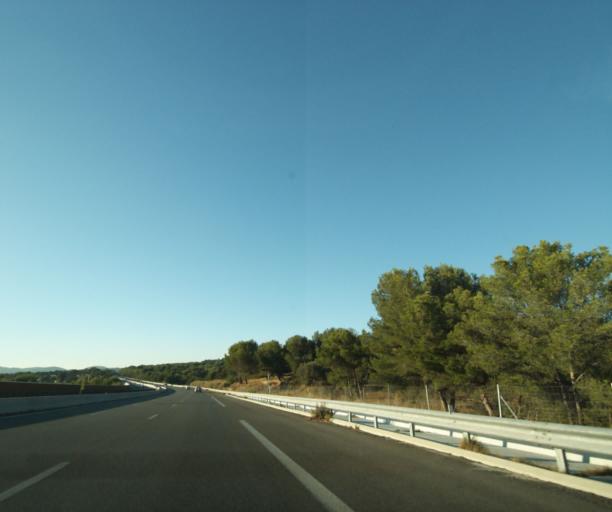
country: FR
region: Provence-Alpes-Cote d'Azur
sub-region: Departement des Bouches-du-Rhone
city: Ceyreste
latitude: 43.1938
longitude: 5.6509
